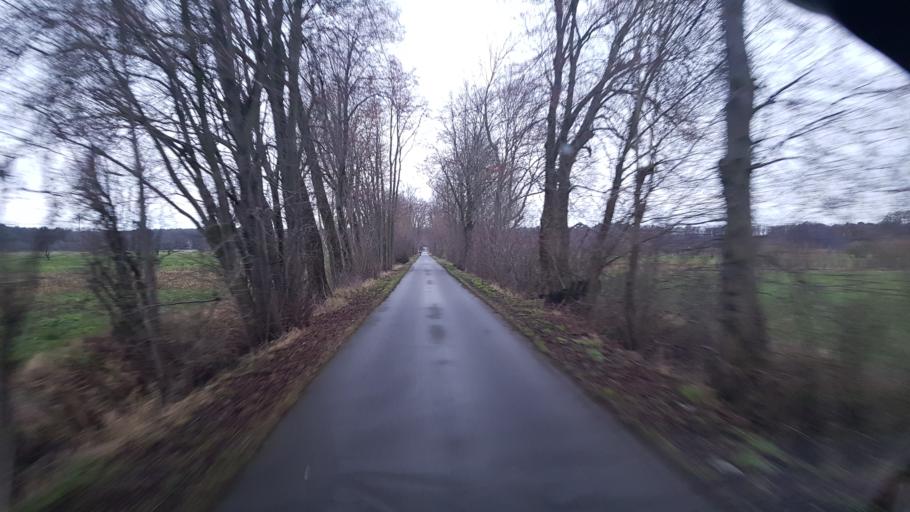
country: DE
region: Brandenburg
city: Ziltendorf
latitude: 52.2178
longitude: 14.6222
